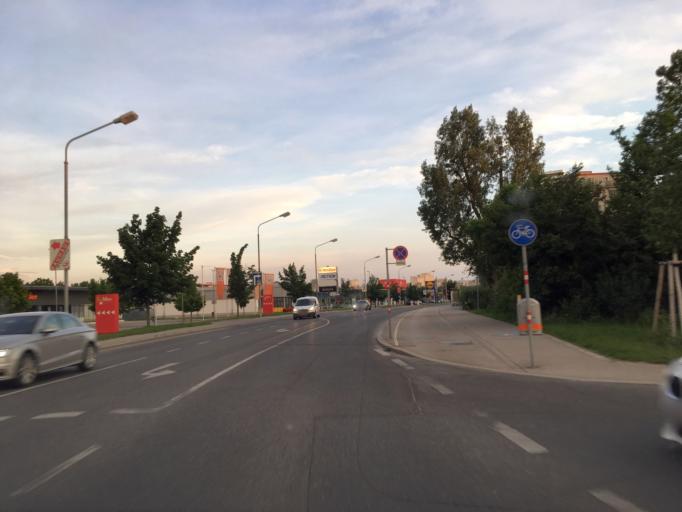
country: AT
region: Lower Austria
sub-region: Politischer Bezirk Wien-Umgebung
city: Gerasdorf bei Wien
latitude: 48.2681
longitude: 16.4565
